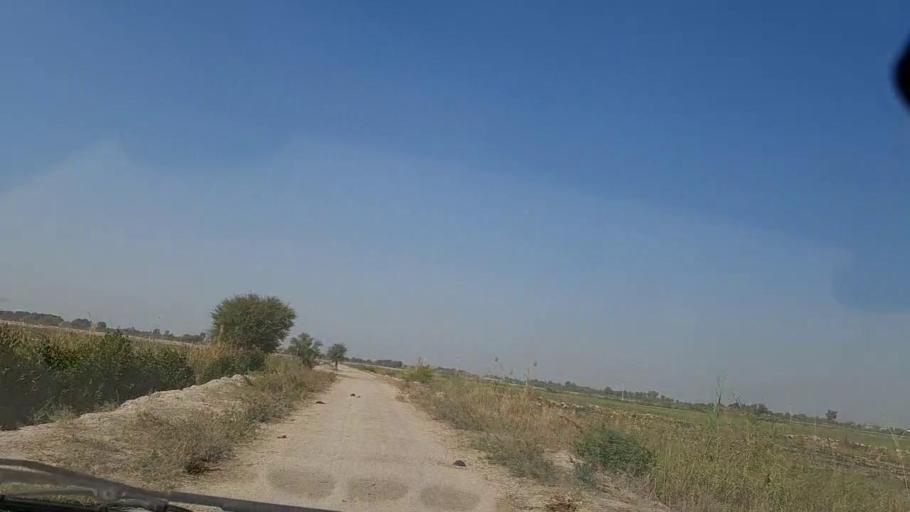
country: PK
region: Sindh
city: Mirpur Khas
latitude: 25.5062
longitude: 68.9116
